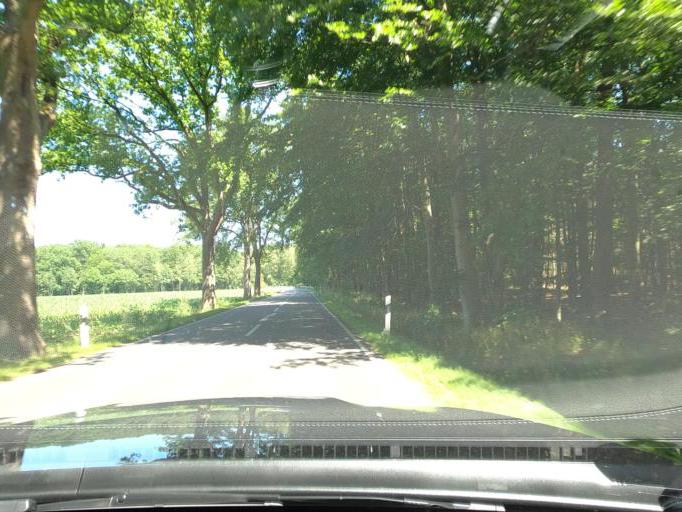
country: DE
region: Lower Saxony
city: Wathlingen
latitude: 52.5006
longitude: 10.1304
